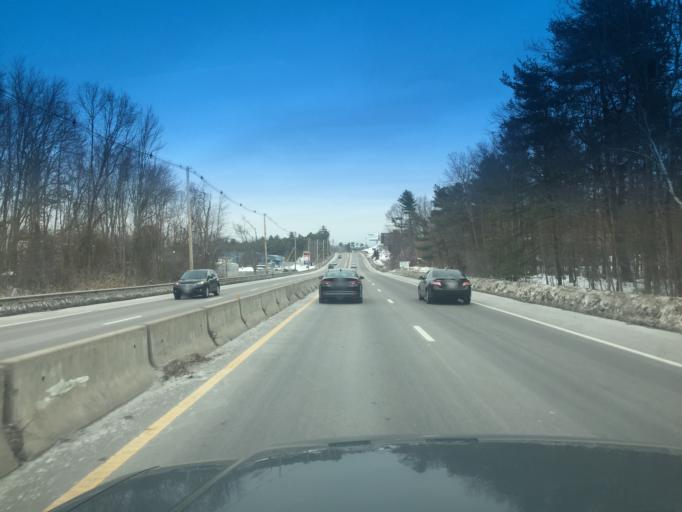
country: US
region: Massachusetts
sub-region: Norfolk County
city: Walpole
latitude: 42.1157
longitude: -71.2386
